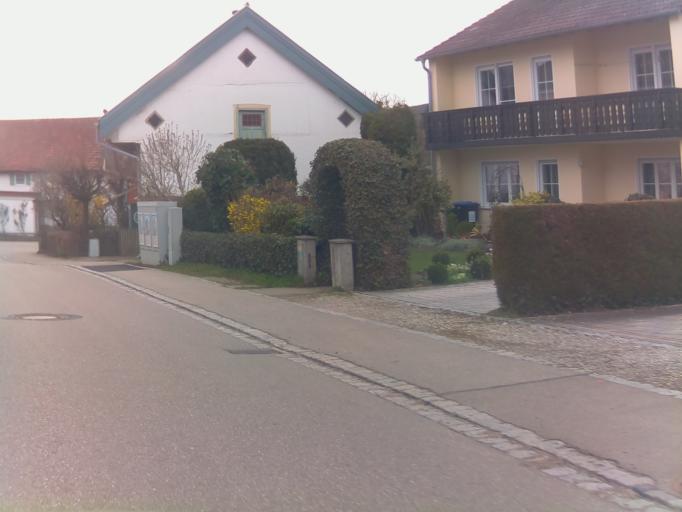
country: DE
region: Bavaria
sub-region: Upper Bavaria
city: Purgen
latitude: 48.0047
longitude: 10.9069
